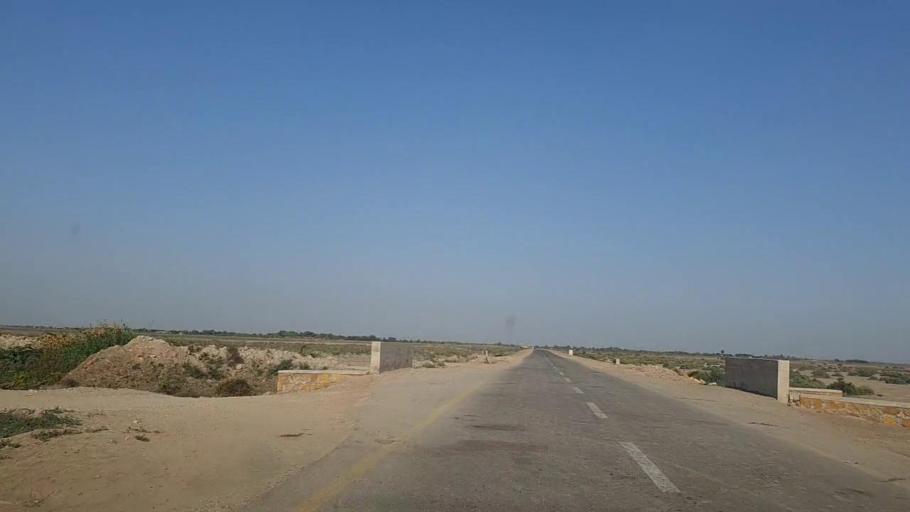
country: PK
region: Sindh
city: Jati
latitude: 24.4435
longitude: 68.3238
